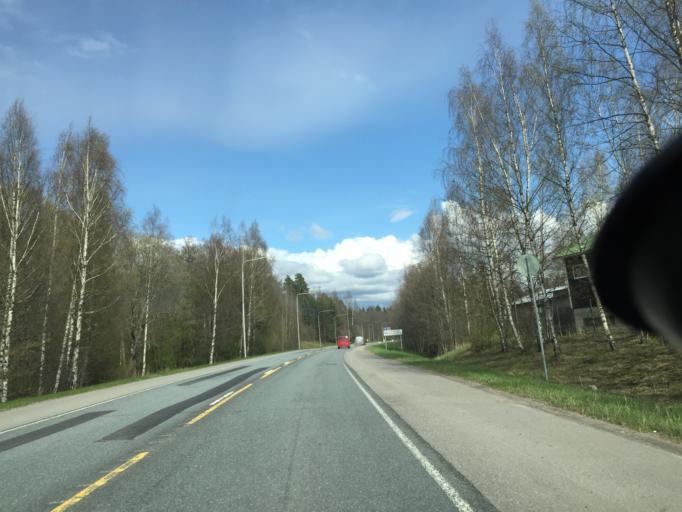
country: FI
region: Uusimaa
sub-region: Raaseporin
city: Ekenaes
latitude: 59.9840
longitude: 23.4576
